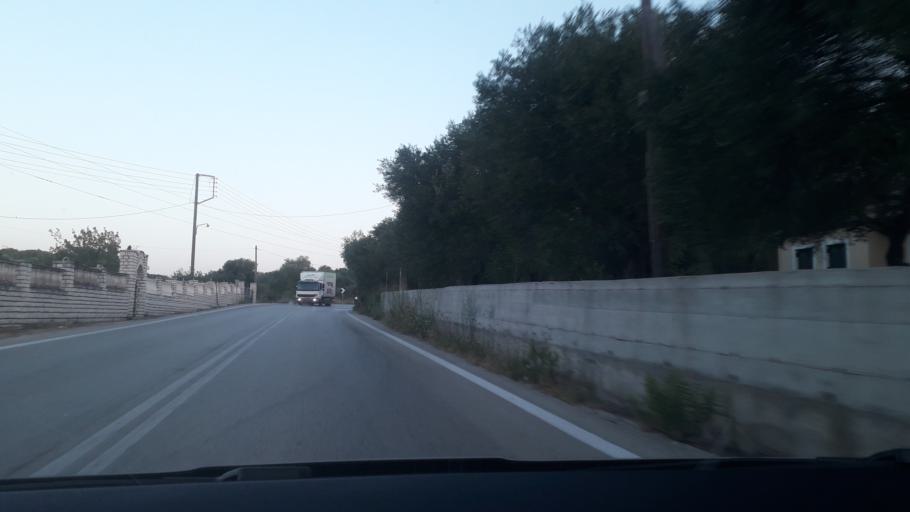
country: GR
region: Ionian Islands
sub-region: Nomos Kerkyras
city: Agios Matthaios
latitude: 39.4573
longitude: 19.9168
